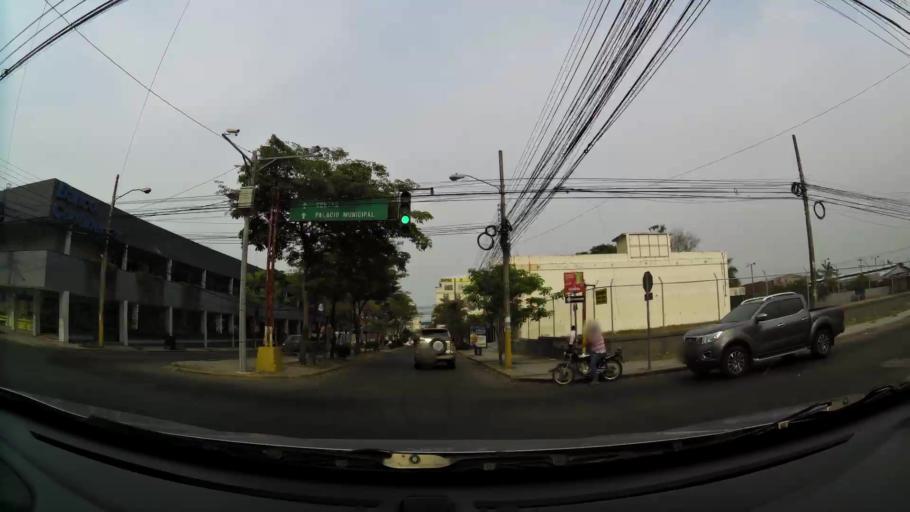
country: HN
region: Cortes
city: San Pedro Sula
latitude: 15.5062
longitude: -88.0303
